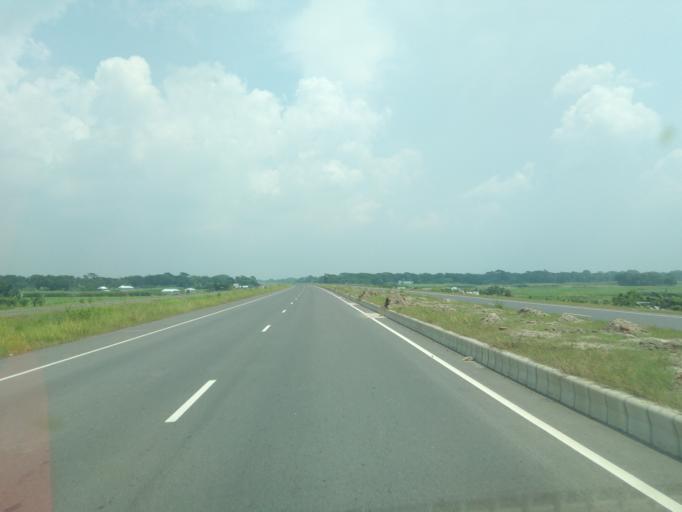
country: BD
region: Dhaka
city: Char Bhadrasan
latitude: 23.3995
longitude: 90.1817
